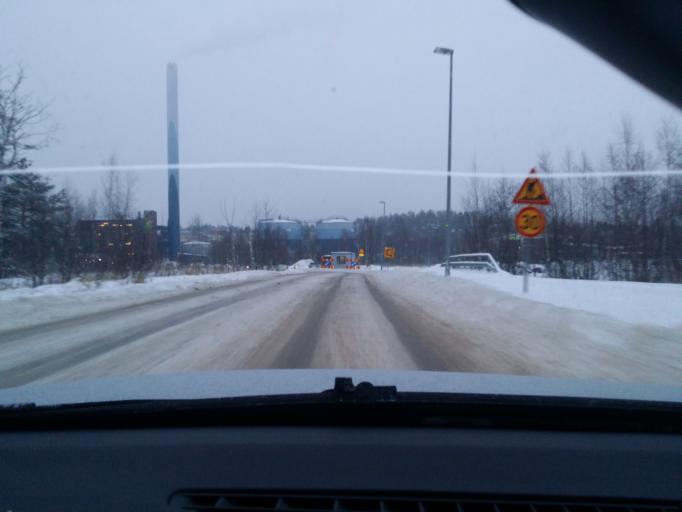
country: FI
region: Uusimaa
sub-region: Helsinki
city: Teekkarikylae
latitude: 60.2155
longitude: 24.8322
